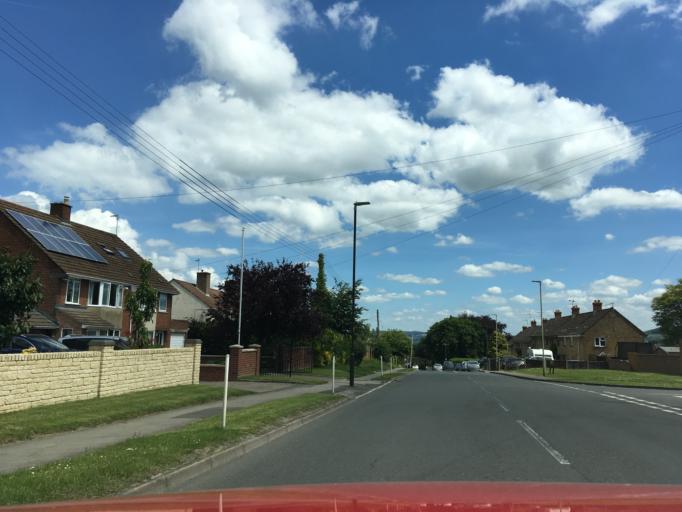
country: GB
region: England
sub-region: Gloucestershire
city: Dursley
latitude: 51.6952
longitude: -2.3721
